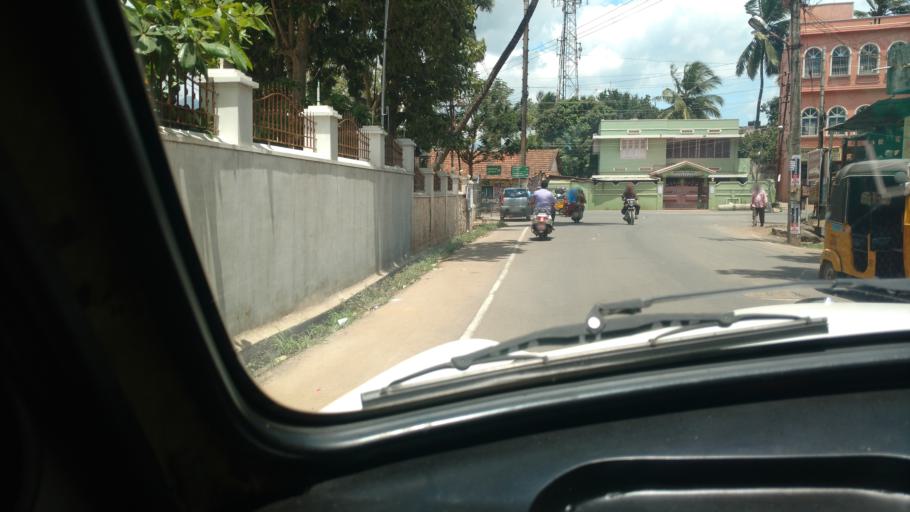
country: IN
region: Tamil Nadu
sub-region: Kanniyakumari
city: Nagercoil
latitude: 8.1890
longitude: 77.4179
